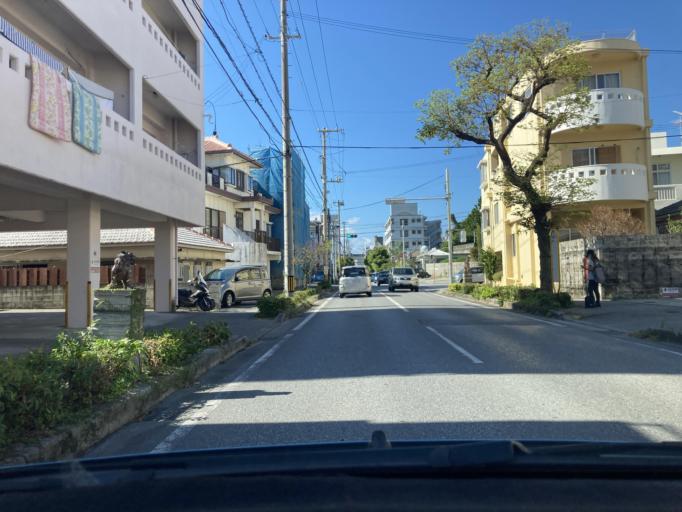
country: JP
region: Okinawa
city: Naha-shi
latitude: 26.2410
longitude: 127.6950
